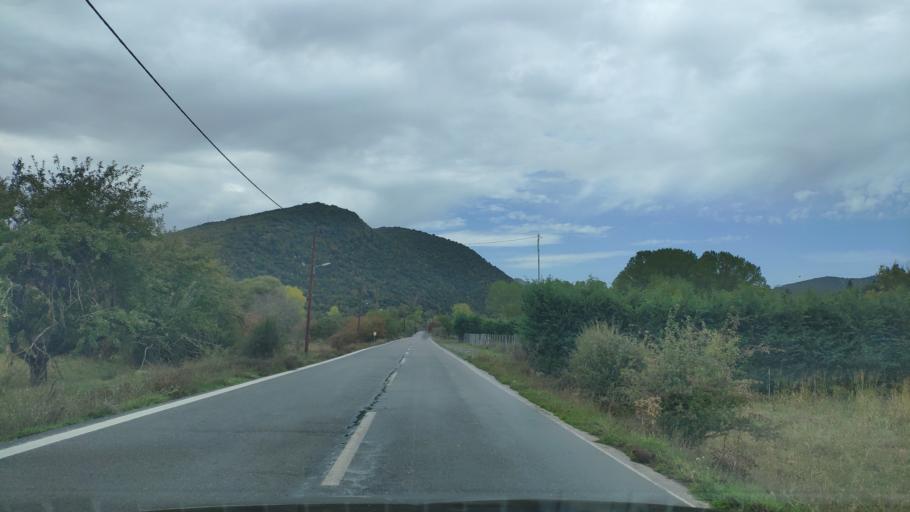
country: GR
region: Peloponnese
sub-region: Nomos Arkadias
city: Dimitsana
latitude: 37.6320
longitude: 22.0805
